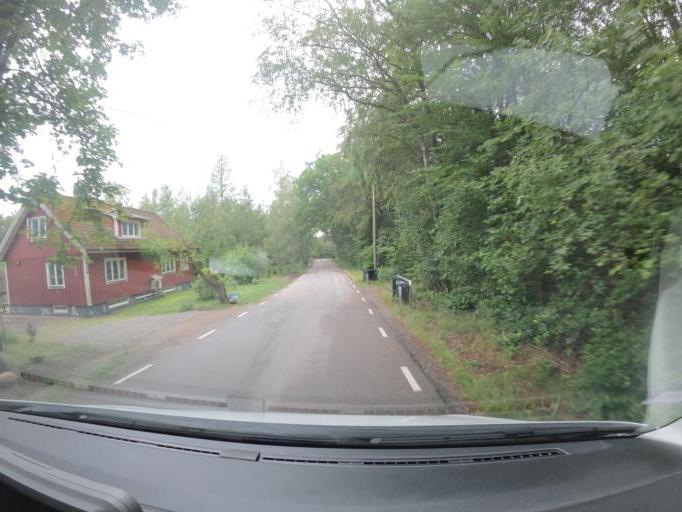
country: SE
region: Skane
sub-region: Klippans Kommun
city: Klippan
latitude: 56.2680
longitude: 13.1383
